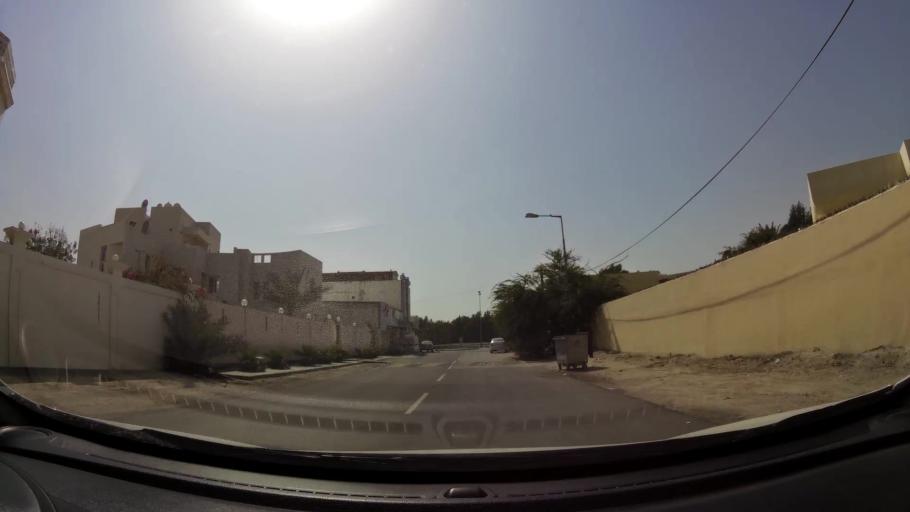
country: BH
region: Manama
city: Jidd Hafs
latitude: 26.1991
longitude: 50.4613
